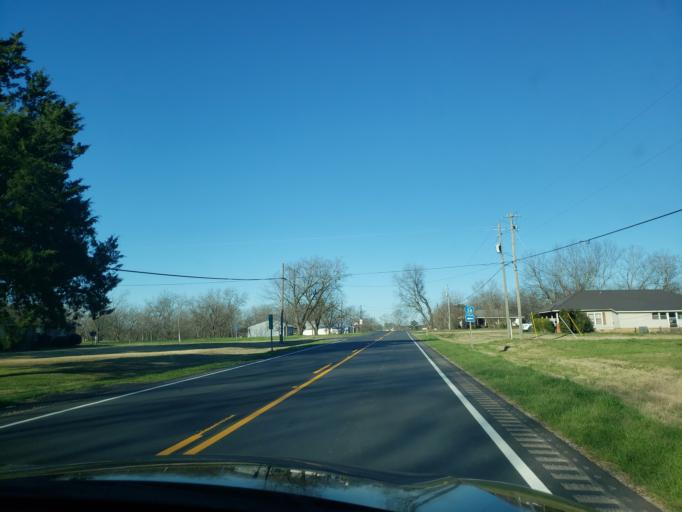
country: US
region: Alabama
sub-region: Macon County
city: Tuskegee
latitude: 32.5822
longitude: -85.7353
